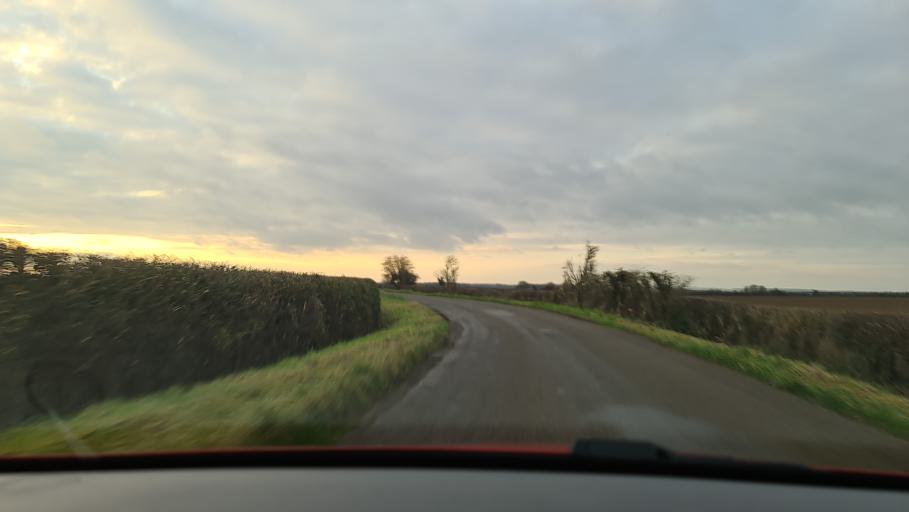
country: GB
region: England
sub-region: Oxfordshire
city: Somerton
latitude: 51.9217
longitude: -1.2738
